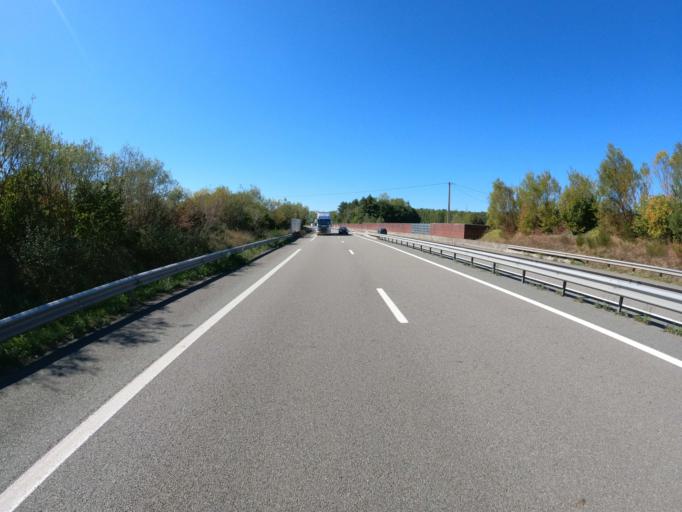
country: FR
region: Limousin
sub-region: Departement de la Creuse
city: Gouzon
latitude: 46.1988
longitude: 2.2470
